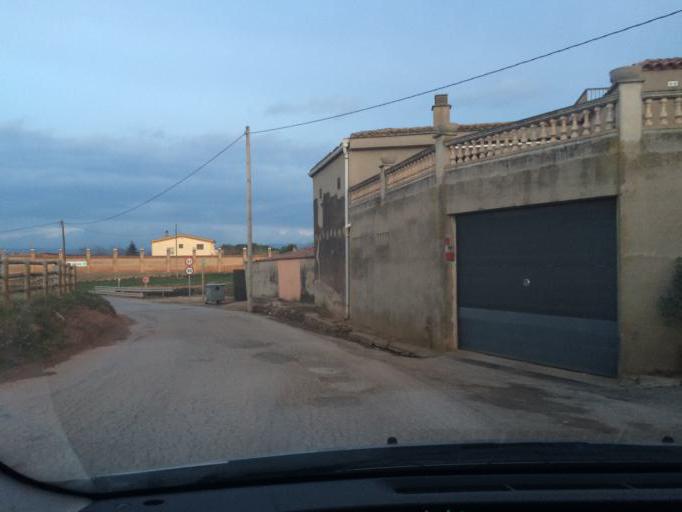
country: ES
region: Catalonia
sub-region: Provincia de Barcelona
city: Sant Fruitos de Bages
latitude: 41.7483
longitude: 1.8471
